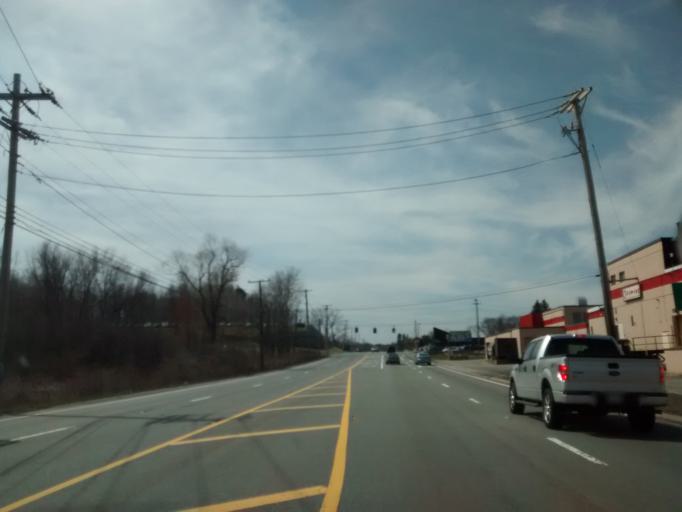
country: US
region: Massachusetts
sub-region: Worcester County
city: Auburn
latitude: 42.1819
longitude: -71.8586
